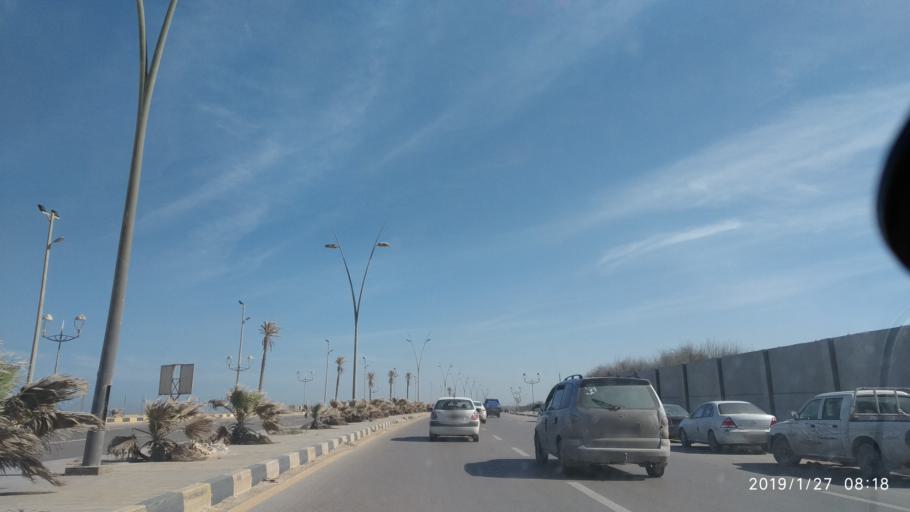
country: LY
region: Tripoli
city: Tagiura
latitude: 32.9084
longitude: 13.2770
